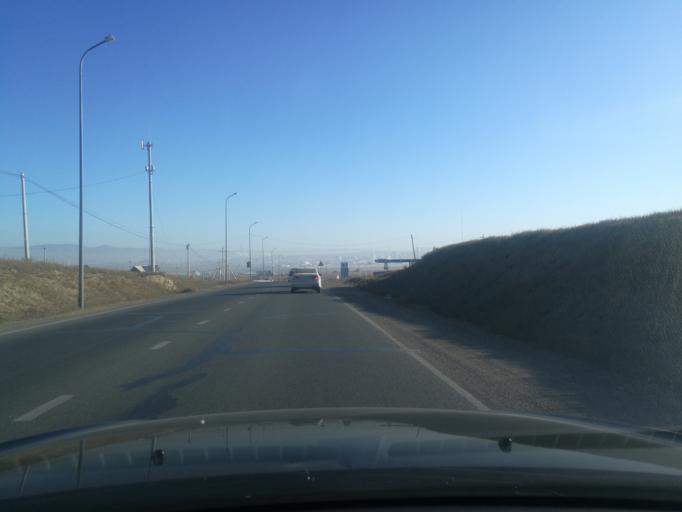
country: MN
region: Ulaanbaatar
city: Ulaanbaatar
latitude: 47.8435
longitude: 106.7278
